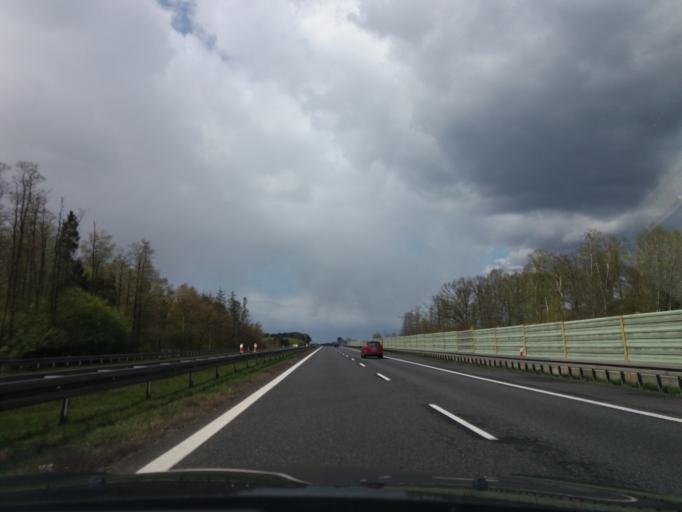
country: PL
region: Silesian Voivodeship
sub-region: Powiat gliwicki
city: Rudziniec
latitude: 50.3722
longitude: 18.4886
